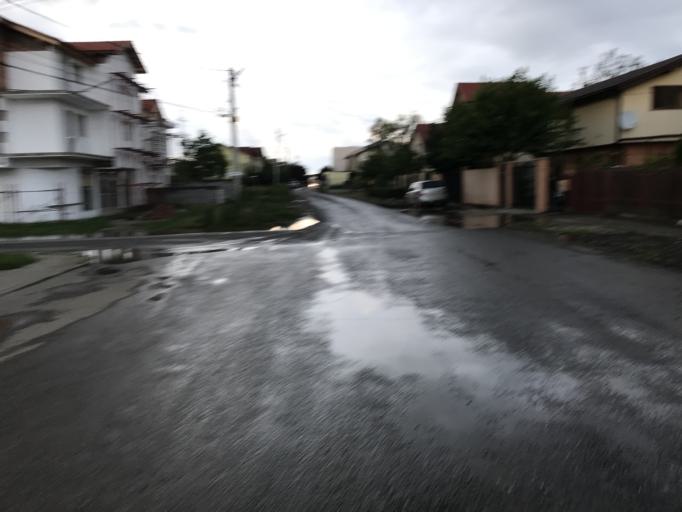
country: RO
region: Timis
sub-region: Comuna Dumbravita
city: Dumbravita
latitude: 45.7870
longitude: 21.2325
